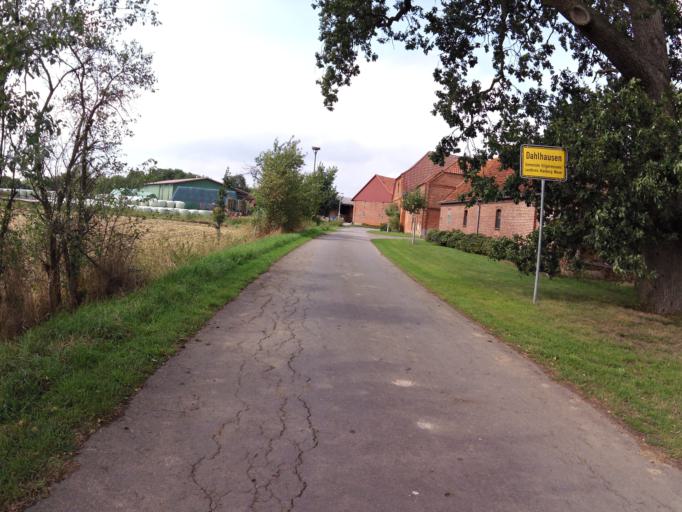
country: DE
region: Lower Saxony
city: Hilgermissen
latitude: 52.8869
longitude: 9.1709
